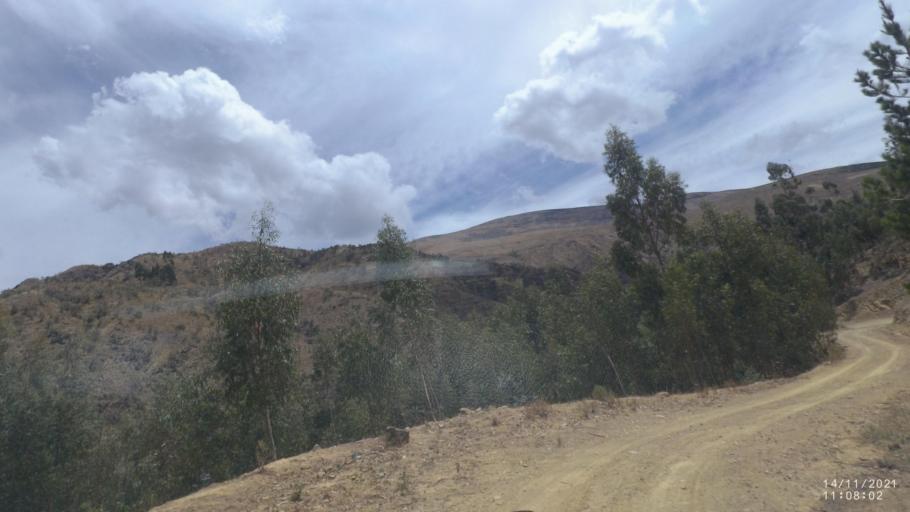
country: BO
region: Cochabamba
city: Cochabamba
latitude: -17.3323
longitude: -66.0547
